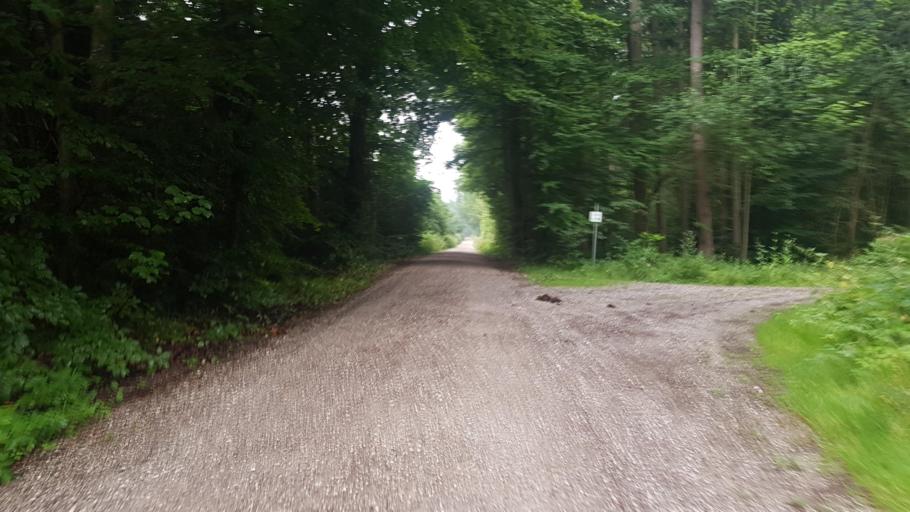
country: DE
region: Bavaria
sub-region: Upper Bavaria
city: Gauting
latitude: 48.0507
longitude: 11.3494
